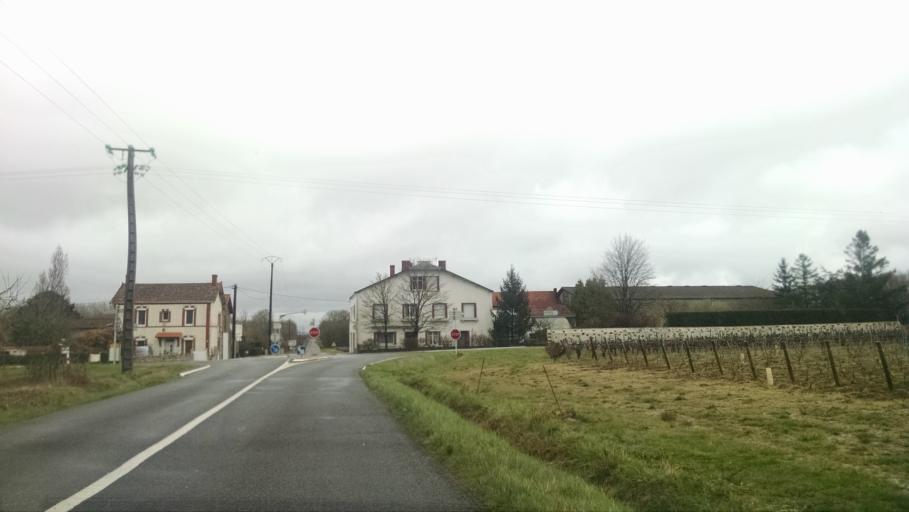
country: FR
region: Pays de la Loire
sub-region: Departement de la Loire-Atlantique
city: Monnieres
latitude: 47.1182
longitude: -1.3648
